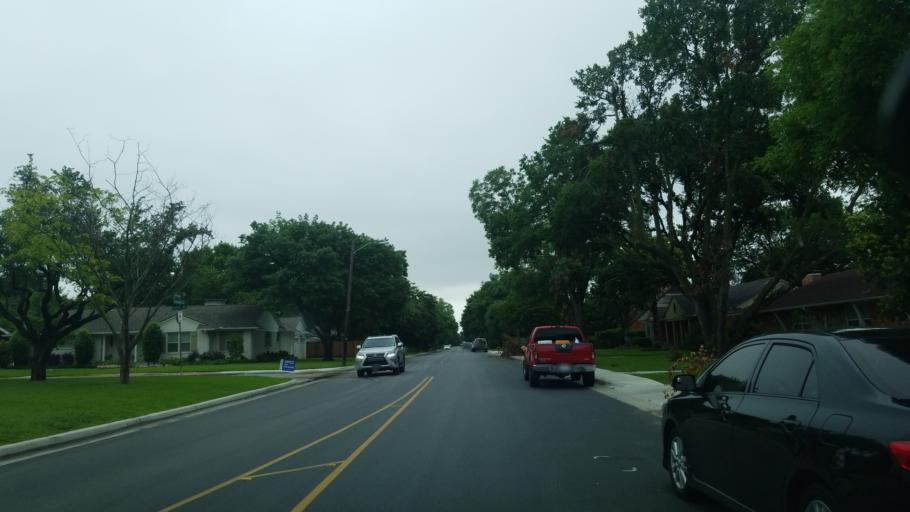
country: US
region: Texas
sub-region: Dallas County
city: Farmers Branch
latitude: 32.8945
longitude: -96.8624
